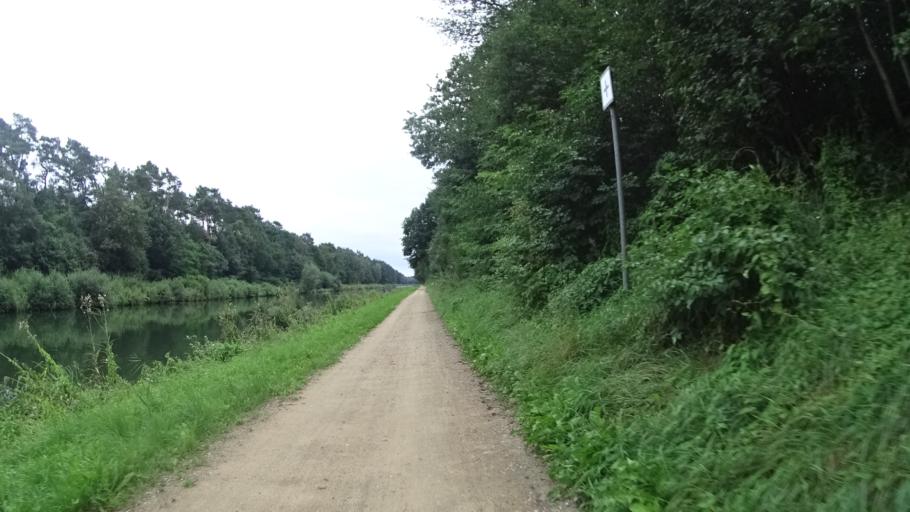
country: DE
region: Schleswig-Holstein
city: Alt Molln
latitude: 53.6009
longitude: 10.6658
